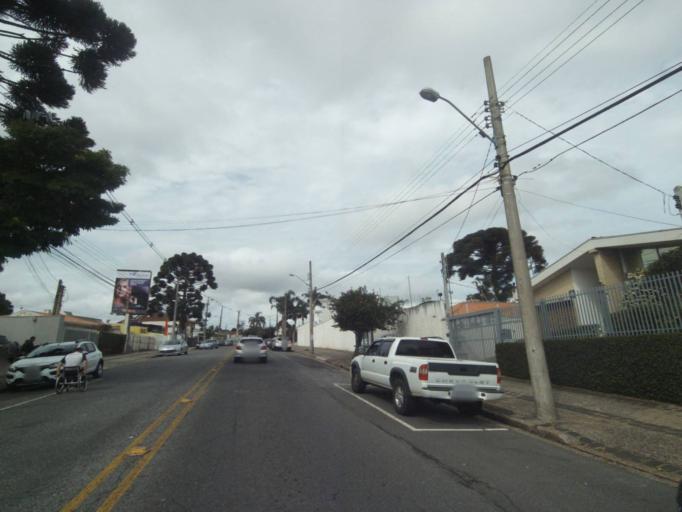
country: BR
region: Parana
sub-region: Curitiba
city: Curitiba
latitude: -25.4449
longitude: -49.3042
